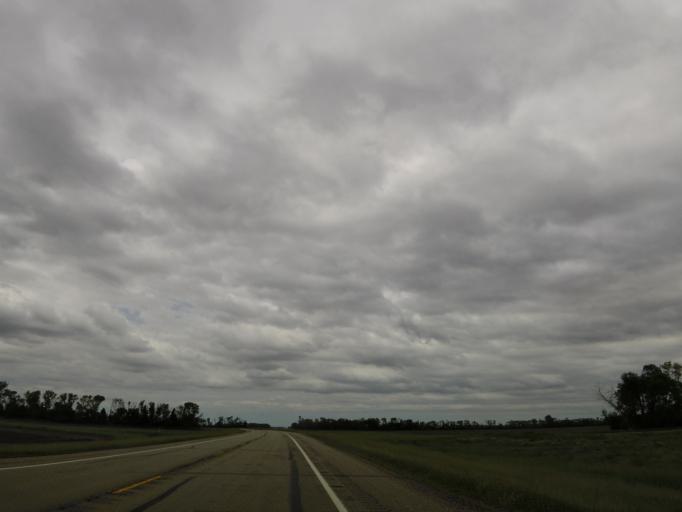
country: US
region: North Dakota
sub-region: Walsh County
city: Grafton
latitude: 48.5346
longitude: -97.4475
